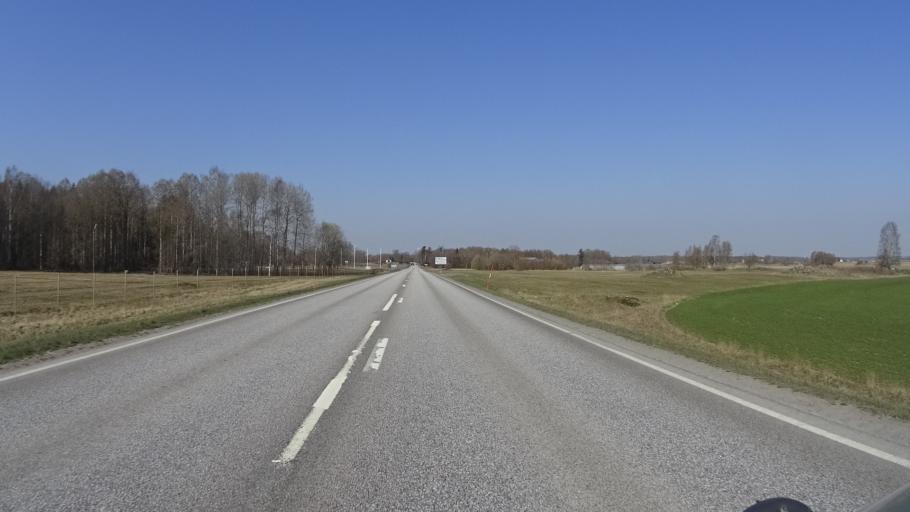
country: SE
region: OEstergoetland
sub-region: Mjolby Kommun
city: Mantorp
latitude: 58.3742
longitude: 15.2879
